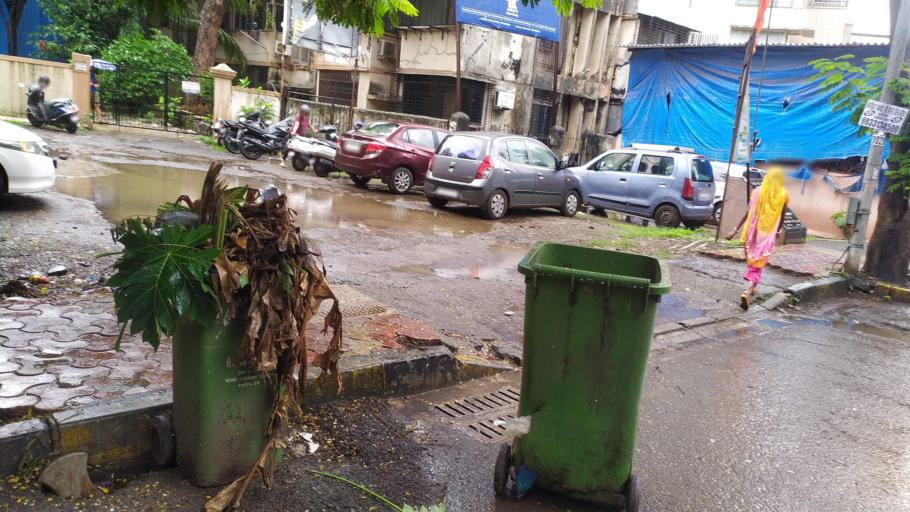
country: IN
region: Maharashtra
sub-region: Mumbai Suburban
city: Borivli
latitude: 19.2363
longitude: 72.8569
